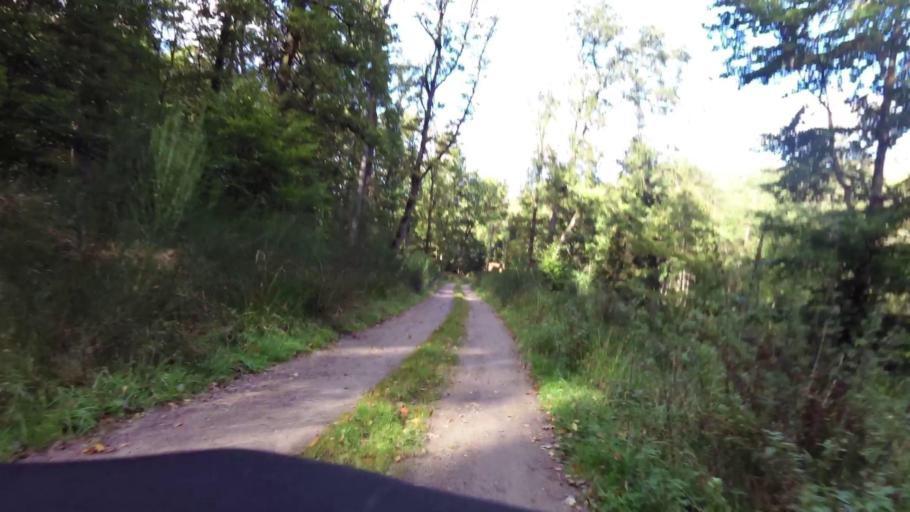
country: PL
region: West Pomeranian Voivodeship
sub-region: Powiat bialogardzki
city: Bialogard
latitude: 54.0416
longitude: 16.1359
